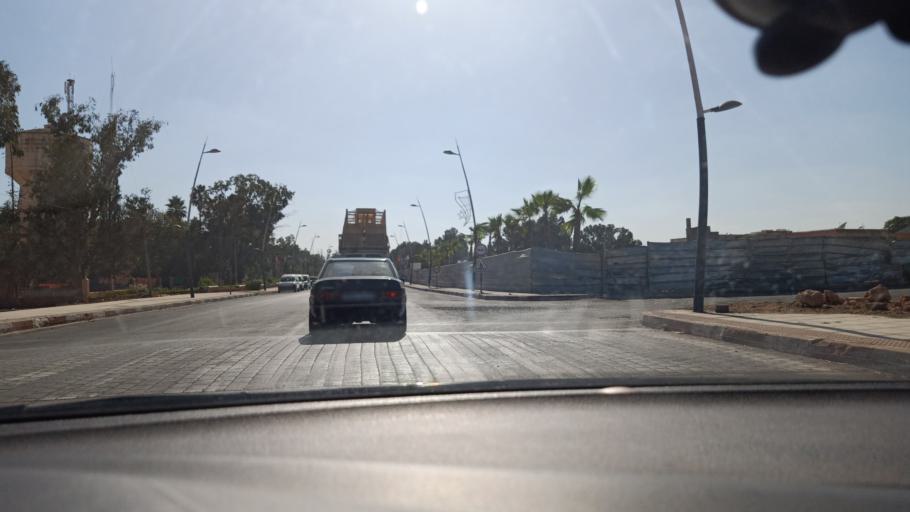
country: MA
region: Doukkala-Abda
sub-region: Safi
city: Youssoufia
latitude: 32.0819
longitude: -8.6215
